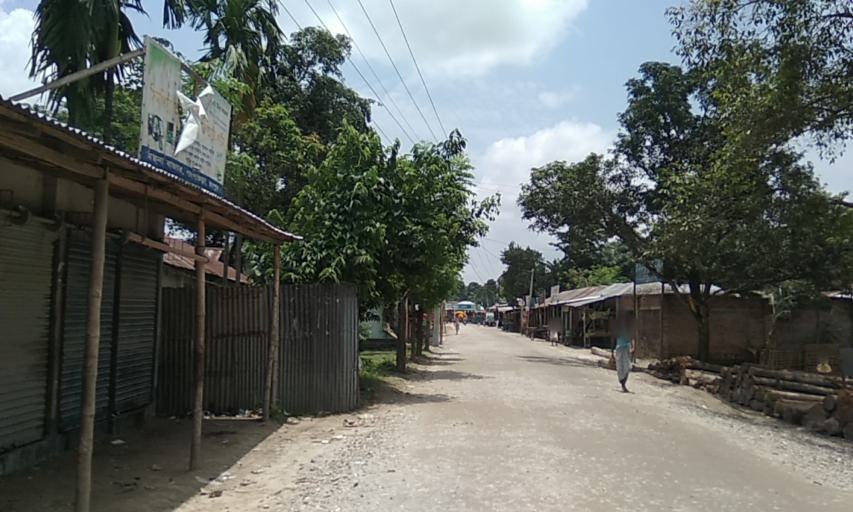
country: BD
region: Rangpur Division
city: Rangpur
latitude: 25.8873
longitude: 89.1859
